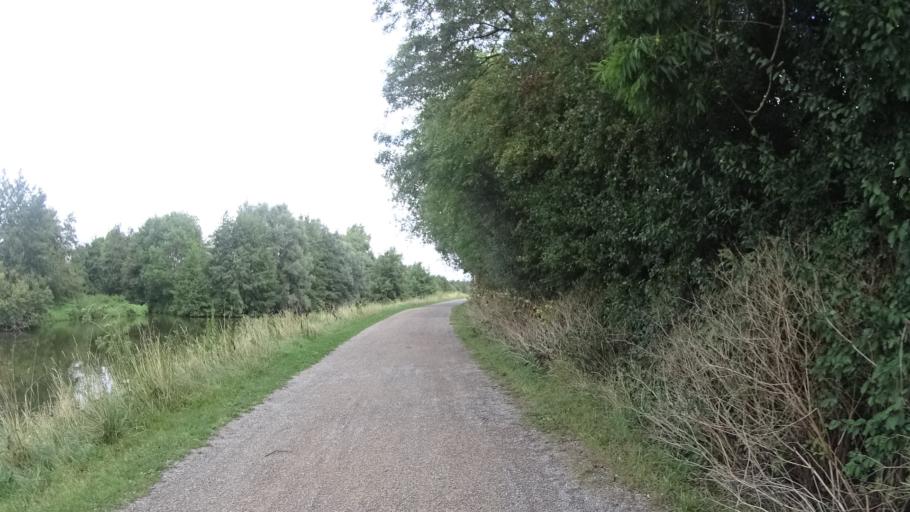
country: FR
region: Nord-Pas-de-Calais
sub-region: Departement du Nord
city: Aulnoye-Aymeries
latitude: 50.2084
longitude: 3.8264
